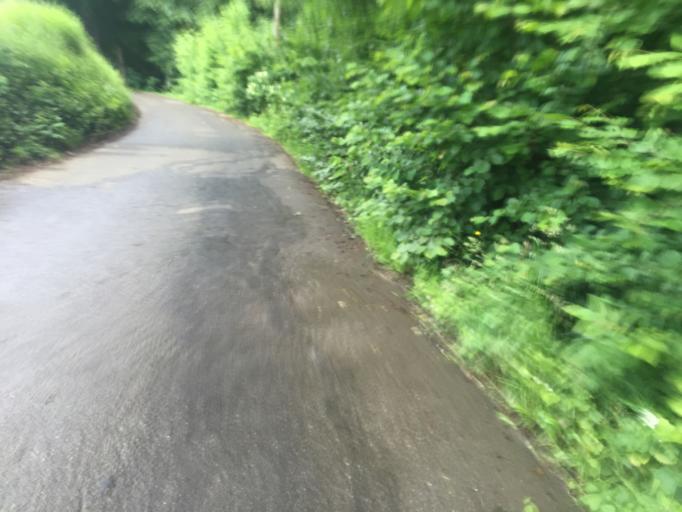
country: CH
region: Bern
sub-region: Bern-Mittelland District
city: Wohlen
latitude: 46.9704
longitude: 7.3739
